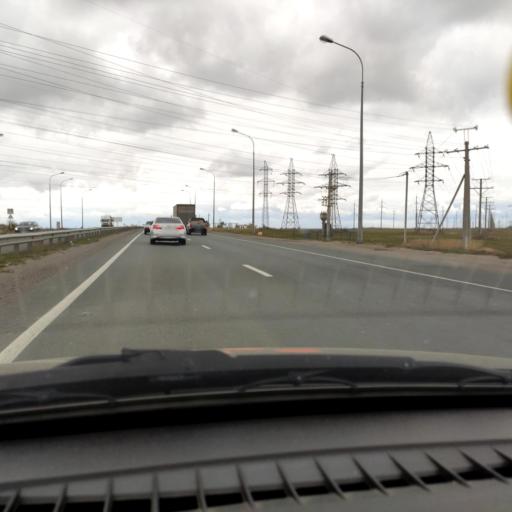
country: RU
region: Samara
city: Zhigulevsk
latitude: 53.5429
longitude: 49.5136
